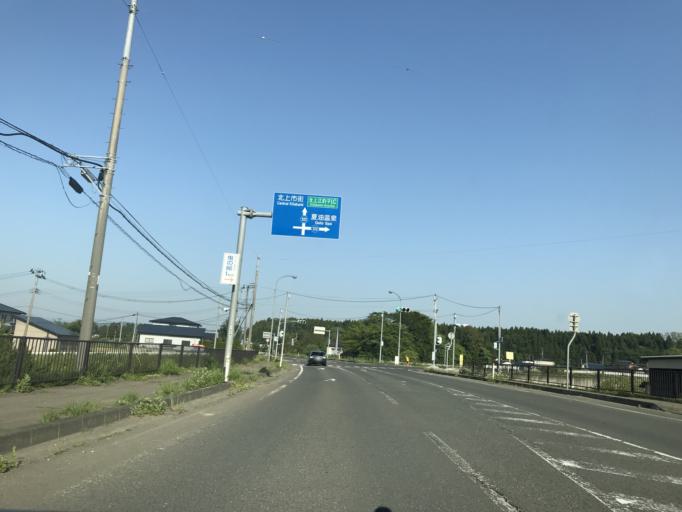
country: JP
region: Iwate
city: Kitakami
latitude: 39.2831
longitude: 141.0505
